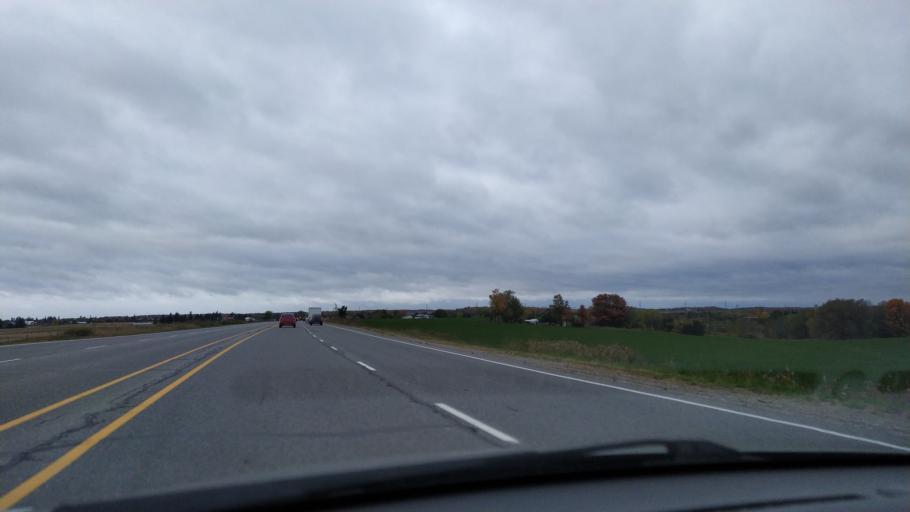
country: CA
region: Ontario
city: Kitchener
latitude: 43.3637
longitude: -80.7233
